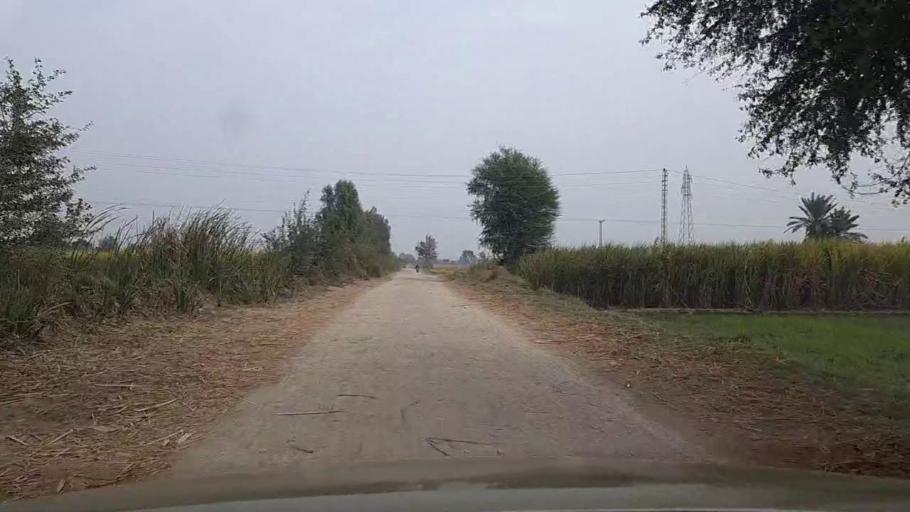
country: PK
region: Sindh
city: Sanghar
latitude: 26.1393
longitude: 68.9518
